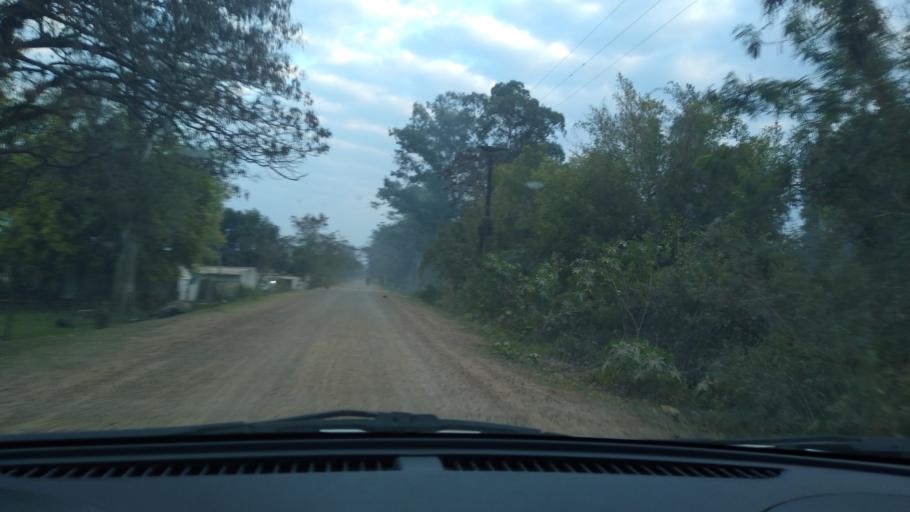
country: AR
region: Chaco
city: Barranqueras
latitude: -27.4624
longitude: -58.9450
